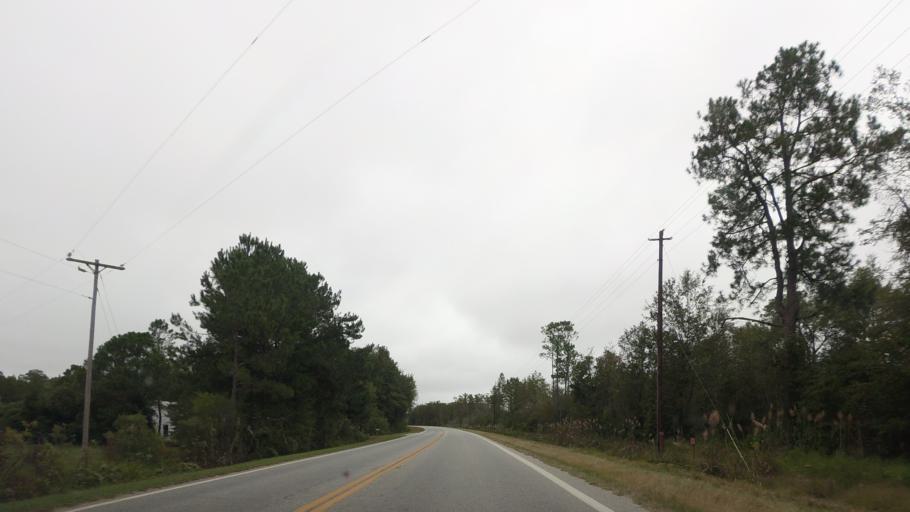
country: US
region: Georgia
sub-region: Berrien County
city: Nashville
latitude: 31.1748
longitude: -83.2333
